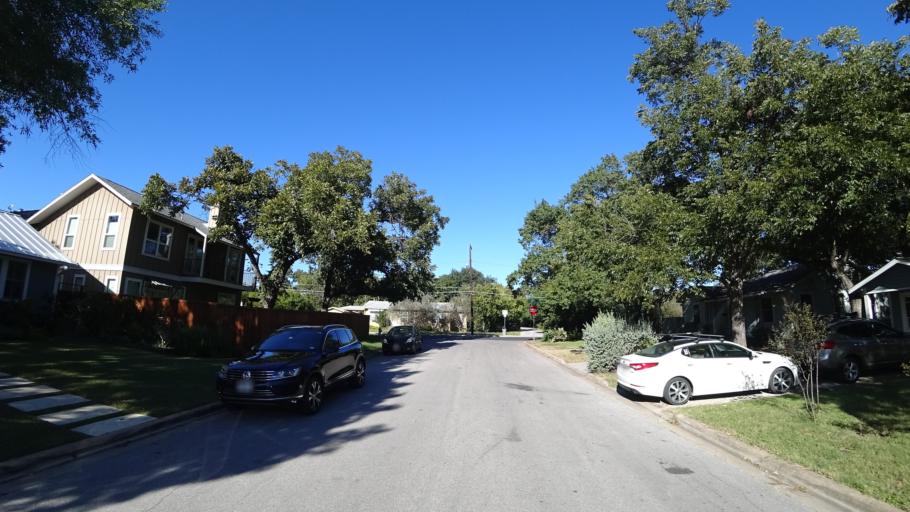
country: US
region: Texas
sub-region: Travis County
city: Austin
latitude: 30.3238
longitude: -97.7300
